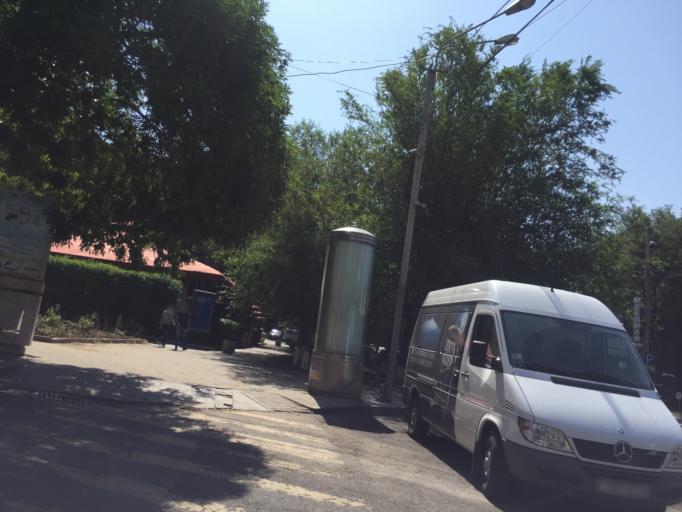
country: AM
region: Yerevan
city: Yerevan
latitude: 40.1886
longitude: 44.5192
